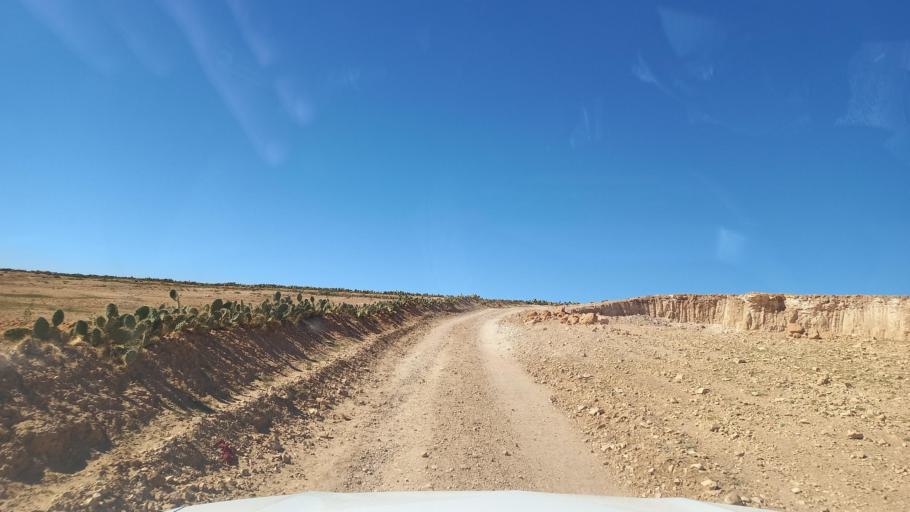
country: TN
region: Al Qasrayn
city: Sbiba
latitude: 35.3789
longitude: 9.0897
